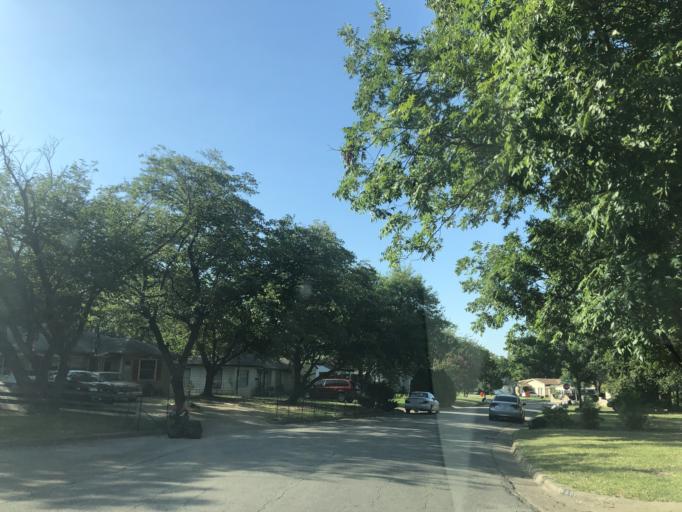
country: US
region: Texas
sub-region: Dallas County
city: Grand Prairie
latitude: 32.7387
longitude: -97.0101
